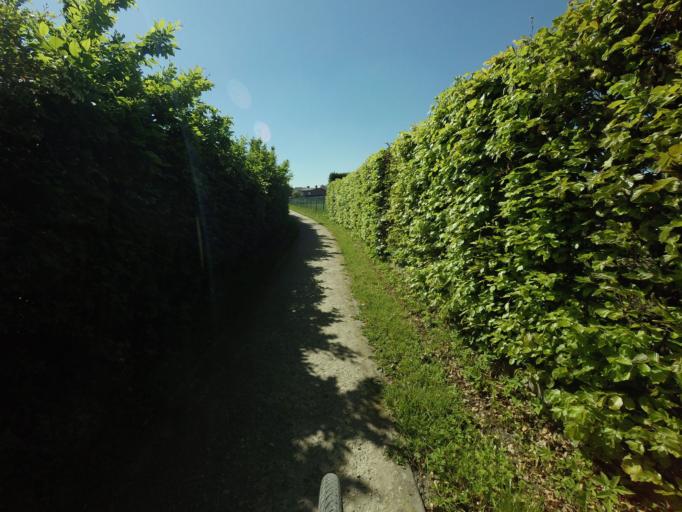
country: BE
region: Flanders
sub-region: Provincie Antwerpen
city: Borsbeek
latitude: 51.1905
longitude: 4.4910
